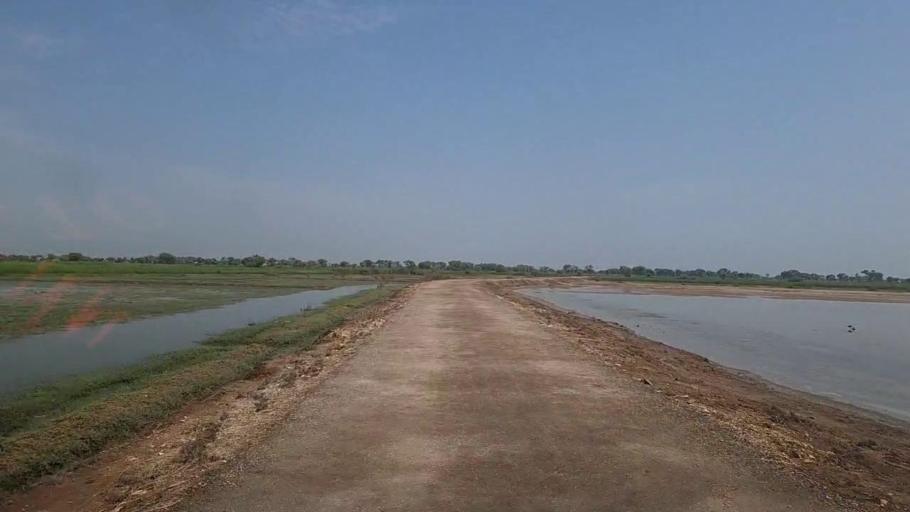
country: PK
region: Sindh
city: Thul
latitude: 28.3013
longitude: 68.6778
